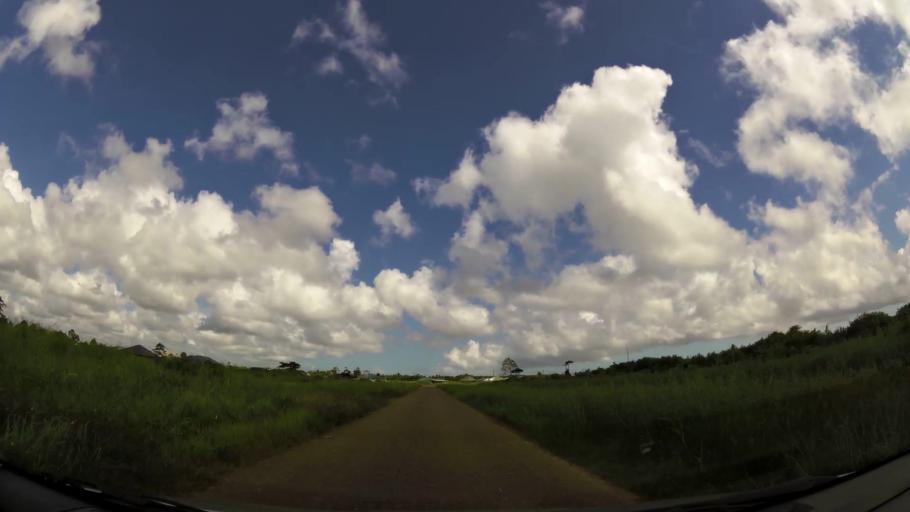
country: SR
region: Paramaribo
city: Paramaribo
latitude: 5.8718
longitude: -55.1297
